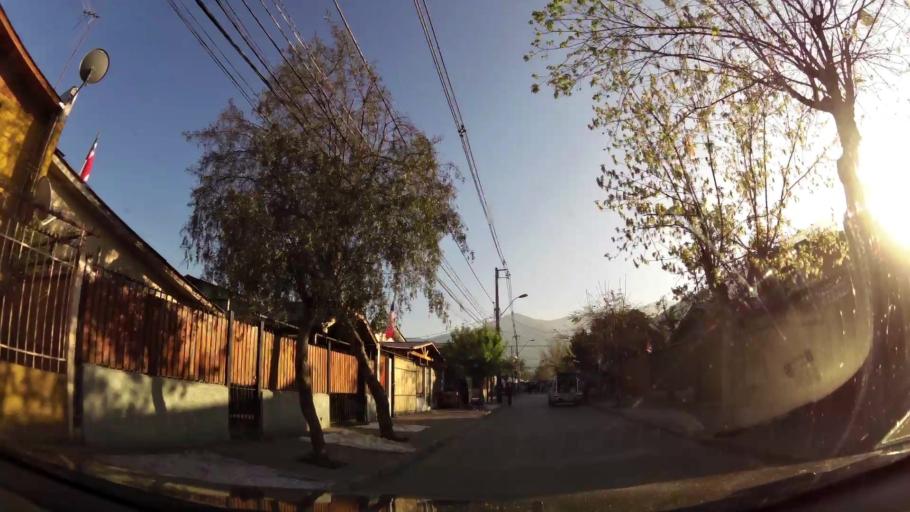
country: CL
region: Santiago Metropolitan
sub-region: Provincia de Santiago
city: Santiago
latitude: -33.3758
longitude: -70.6339
